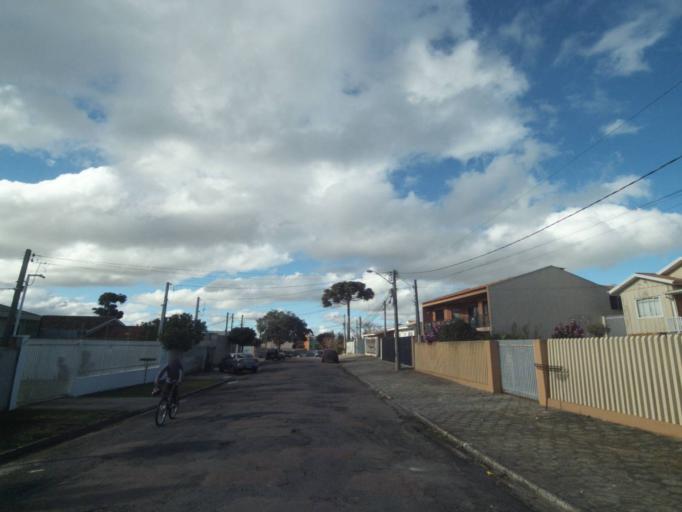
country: BR
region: Parana
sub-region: Sao Jose Dos Pinhais
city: Sao Jose dos Pinhais
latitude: -25.5289
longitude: -49.2899
